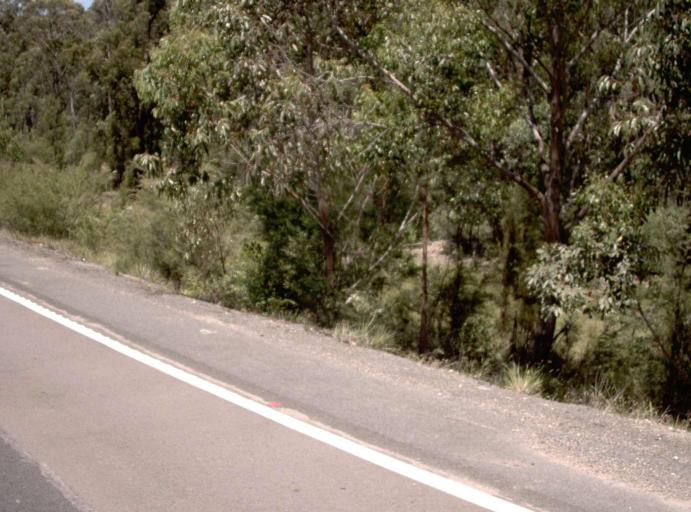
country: AU
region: Victoria
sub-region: East Gippsland
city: Lakes Entrance
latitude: -37.7451
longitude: 148.3883
